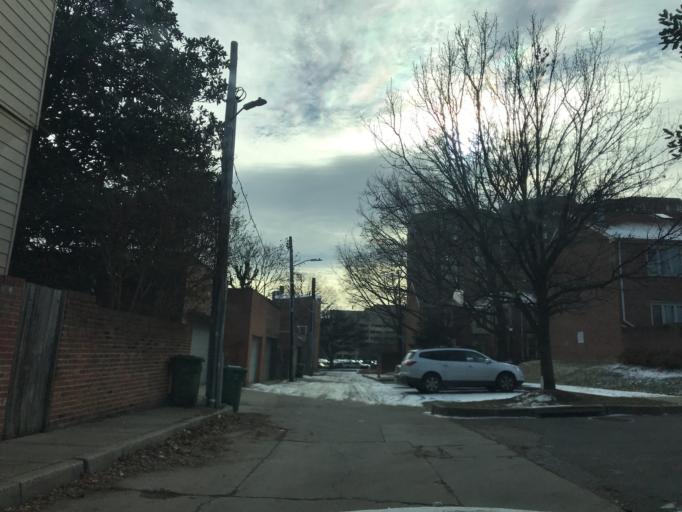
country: US
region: Maryland
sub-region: City of Baltimore
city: Baltimore
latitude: 39.3050
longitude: -76.6245
